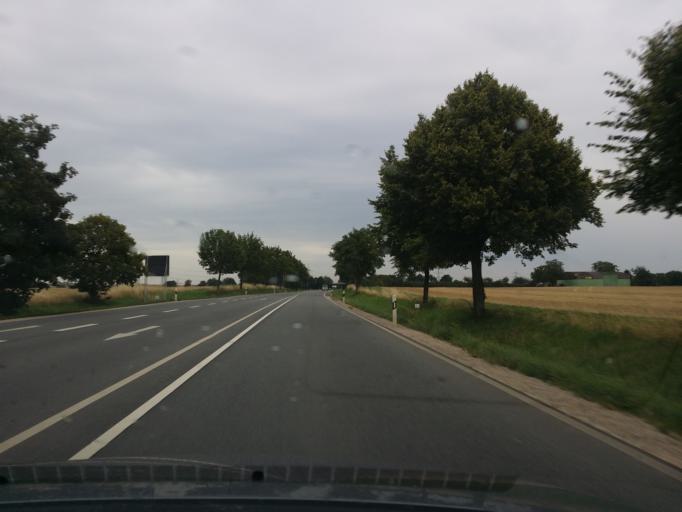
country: DE
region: Hesse
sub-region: Regierungsbezirk Darmstadt
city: Hochheim am Main
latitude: 50.0253
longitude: 8.3555
